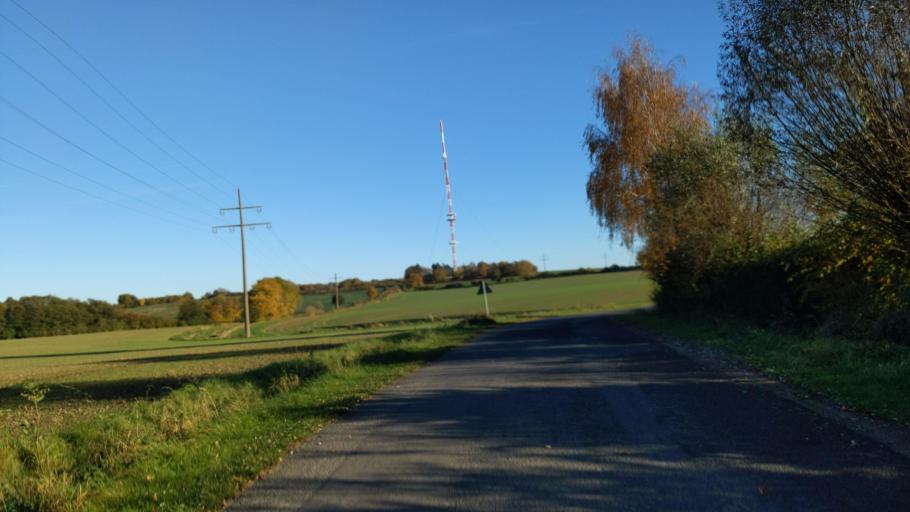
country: DE
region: Schleswig-Holstein
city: Gross Disnack
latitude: 53.7453
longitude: 10.6951
